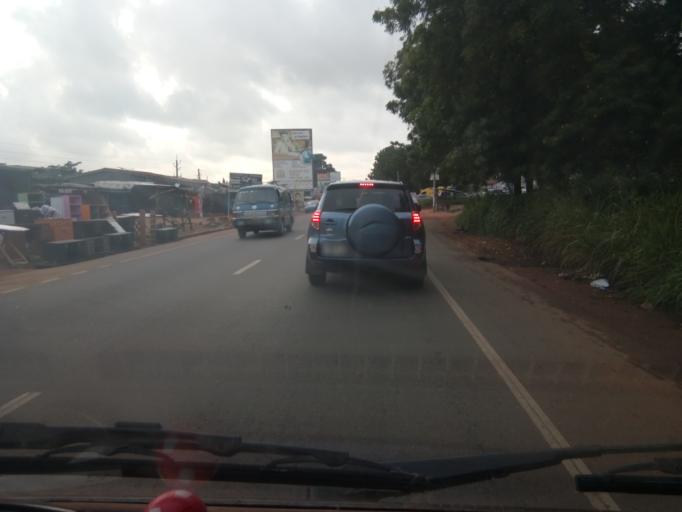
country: GH
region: Greater Accra
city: Medina Estates
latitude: 5.6674
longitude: -0.1832
